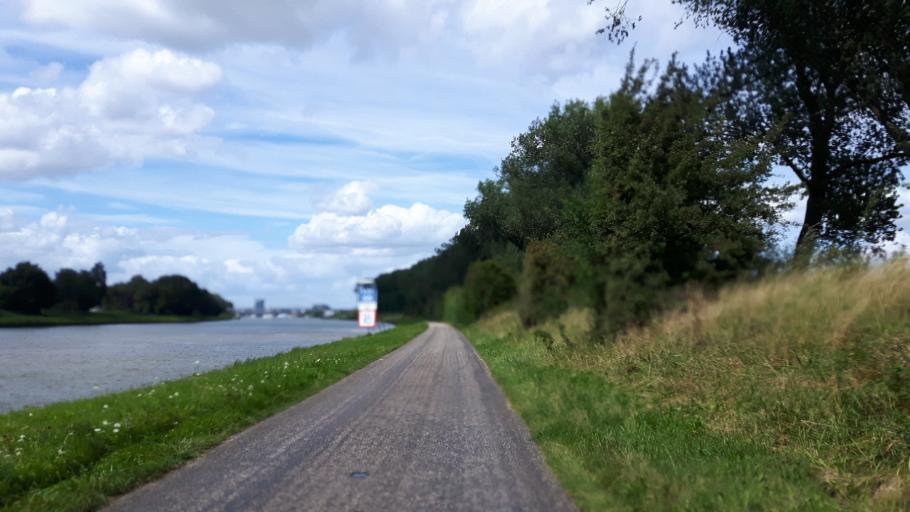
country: NL
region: Utrecht
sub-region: Gemeente Nieuwegein
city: Nieuwegein
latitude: 52.0274
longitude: 5.1154
